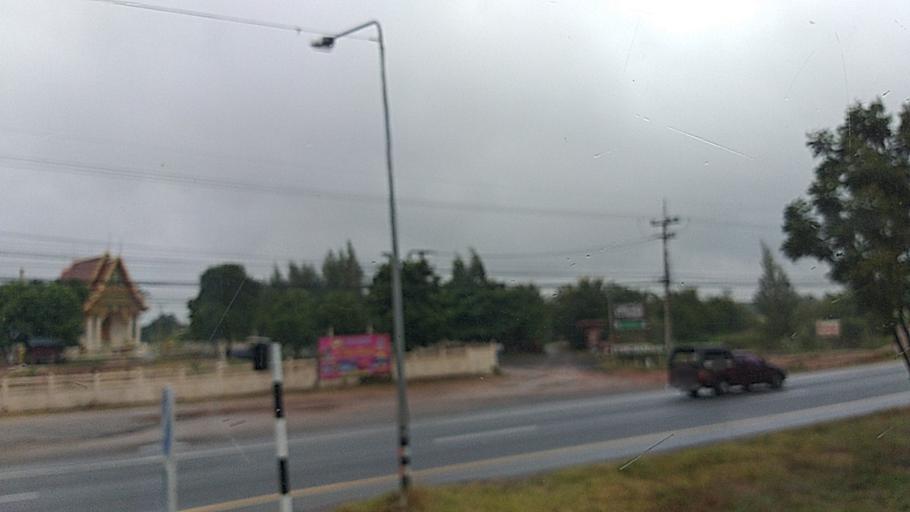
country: TH
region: Nakhon Ratchasima
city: Non Sung
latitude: 15.1696
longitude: 102.3346
